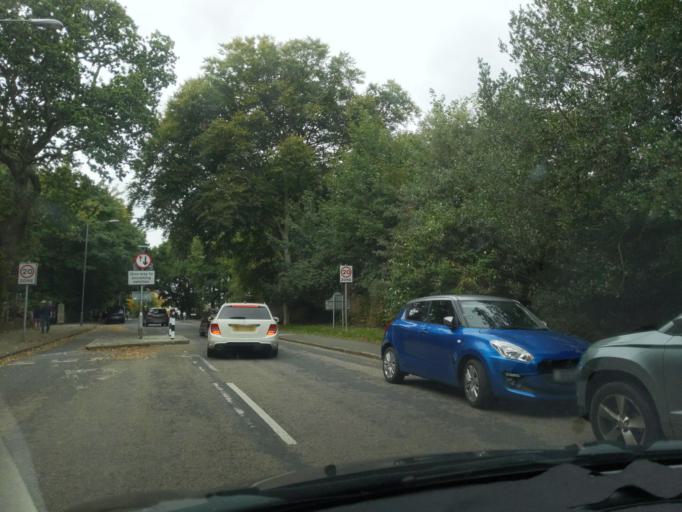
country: GB
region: England
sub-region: Cornwall
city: St Austell
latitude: 50.3367
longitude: -4.7642
